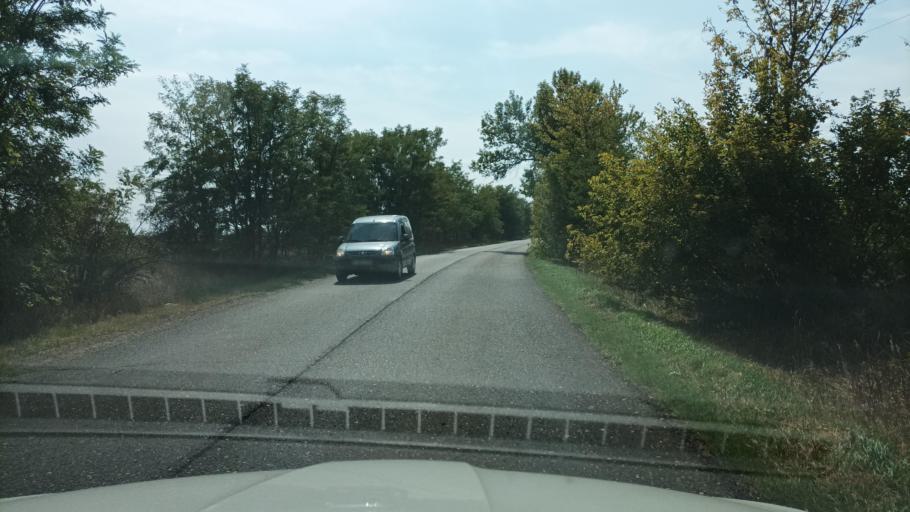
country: HU
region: Heves
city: Hatvan
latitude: 47.6443
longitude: 19.6434
